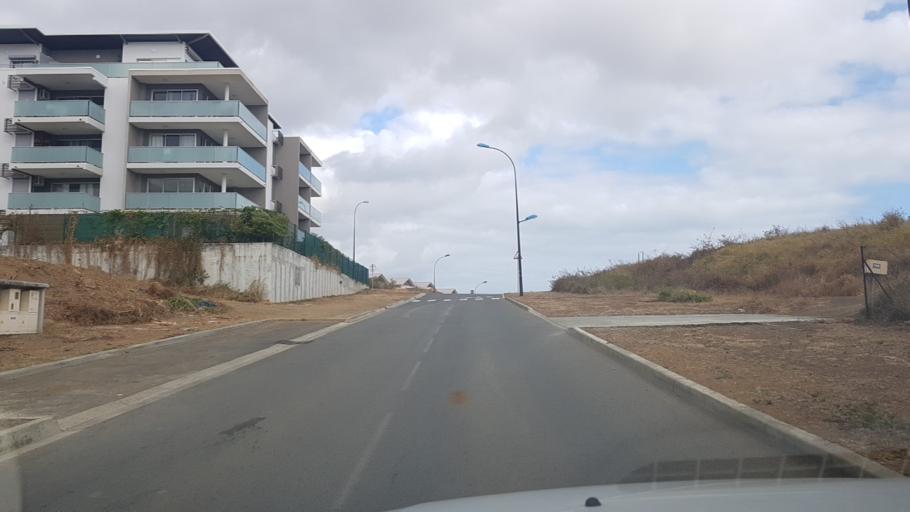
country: NC
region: South Province
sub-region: Dumbea
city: Dumbea
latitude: -22.2030
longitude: 166.4431
